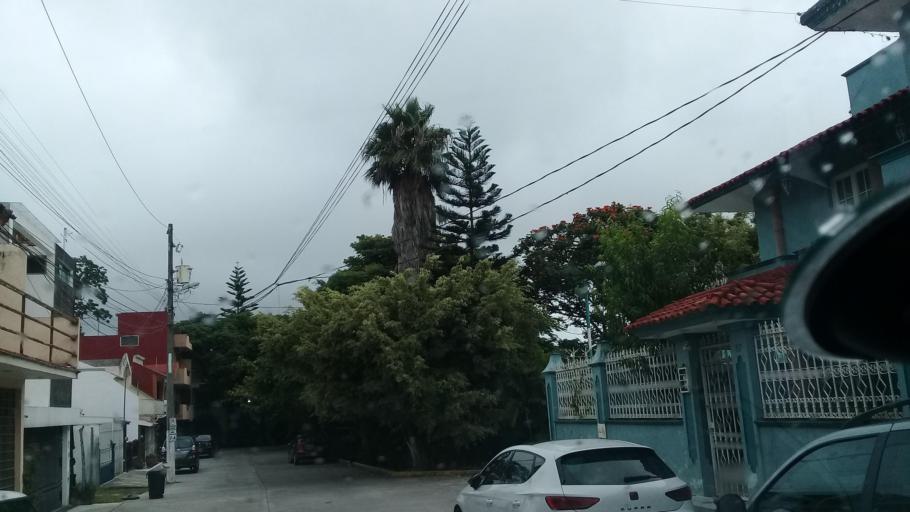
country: MX
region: Veracruz
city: El Castillo
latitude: 19.5335
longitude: -96.8860
